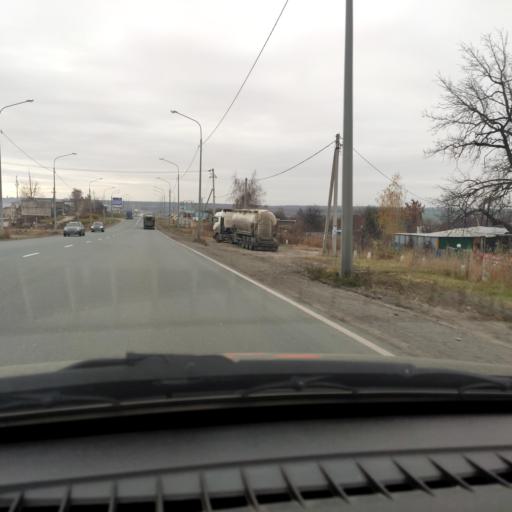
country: RU
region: Samara
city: Zhigulevsk
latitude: 53.3767
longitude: 49.4564
